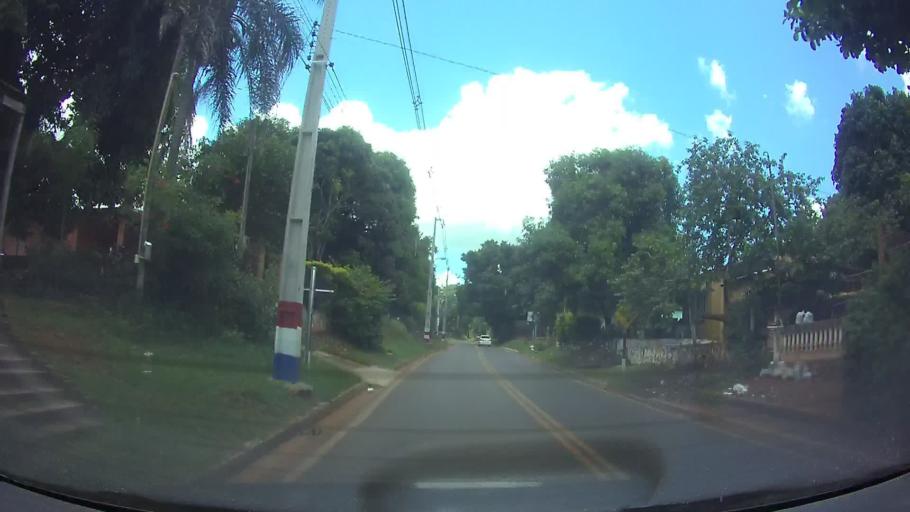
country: PY
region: Central
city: Capiata
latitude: -25.3395
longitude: -57.4178
